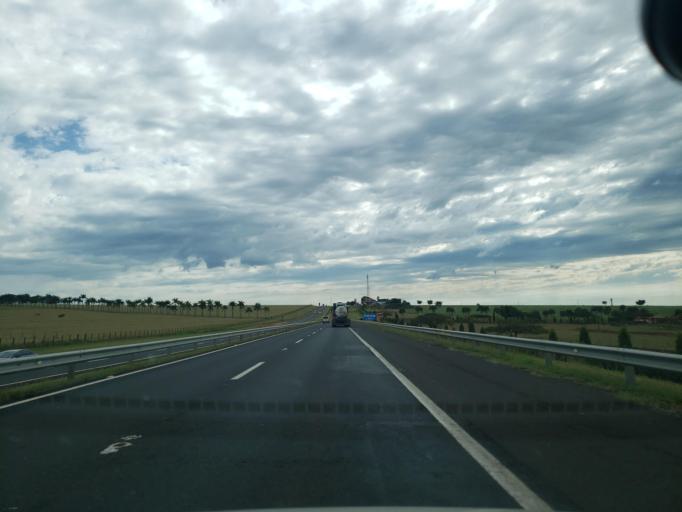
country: BR
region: Sao Paulo
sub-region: Bauru
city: Bauru
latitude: -22.1916
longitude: -49.2056
